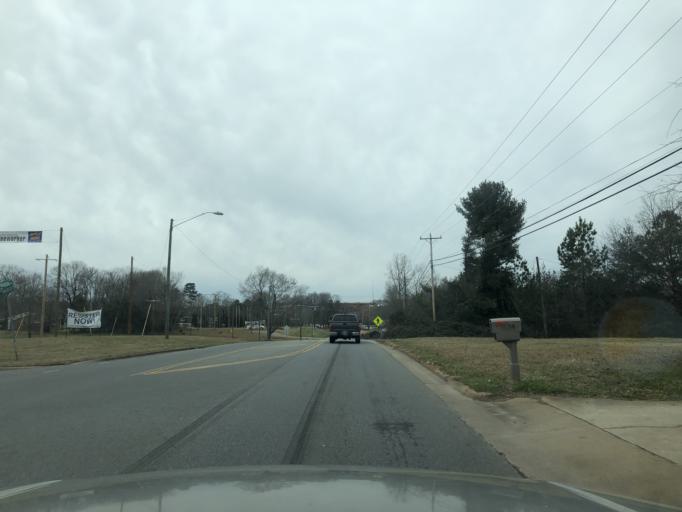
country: US
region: North Carolina
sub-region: Cleveland County
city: Shelby
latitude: 35.2755
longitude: -81.4849
